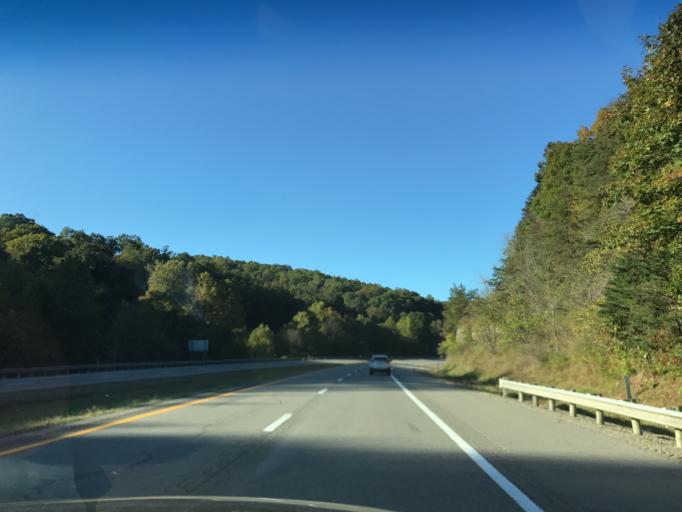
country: US
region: Ohio
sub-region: Washington County
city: Newport
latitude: 39.2561
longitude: -81.2951
